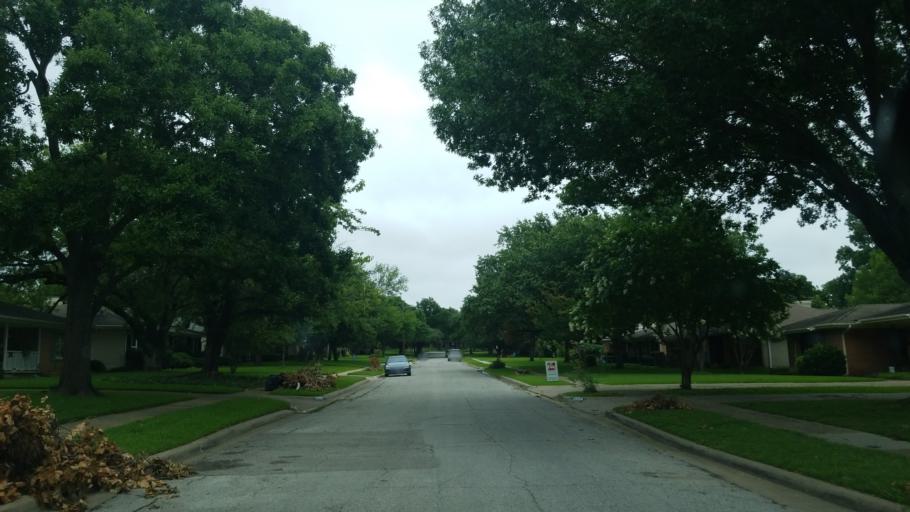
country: US
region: Texas
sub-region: Dallas County
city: Farmers Branch
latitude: 32.8981
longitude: -96.8601
